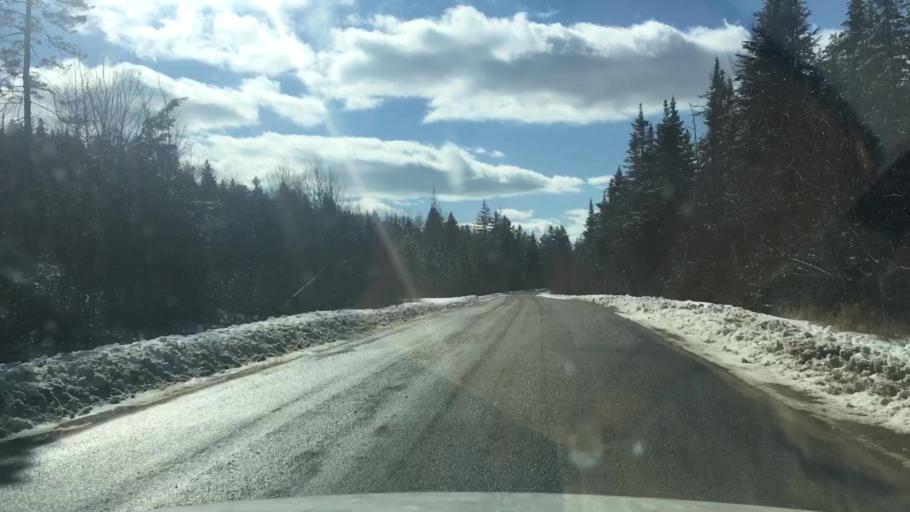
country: US
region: Maine
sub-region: Washington County
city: Machiasport
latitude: 44.6762
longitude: -67.4183
